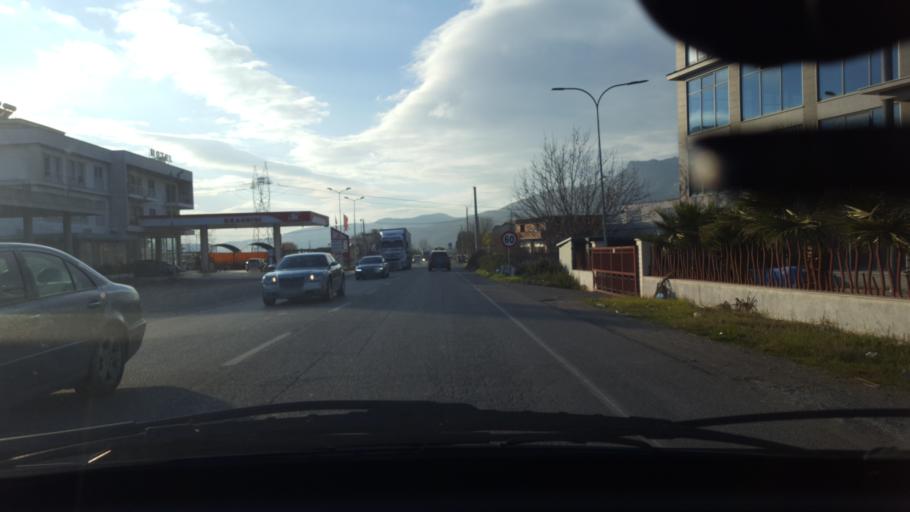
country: AL
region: Elbasan
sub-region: Rrethi i Elbasanit
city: Bradashesh
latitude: 41.1000
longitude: 20.0473
